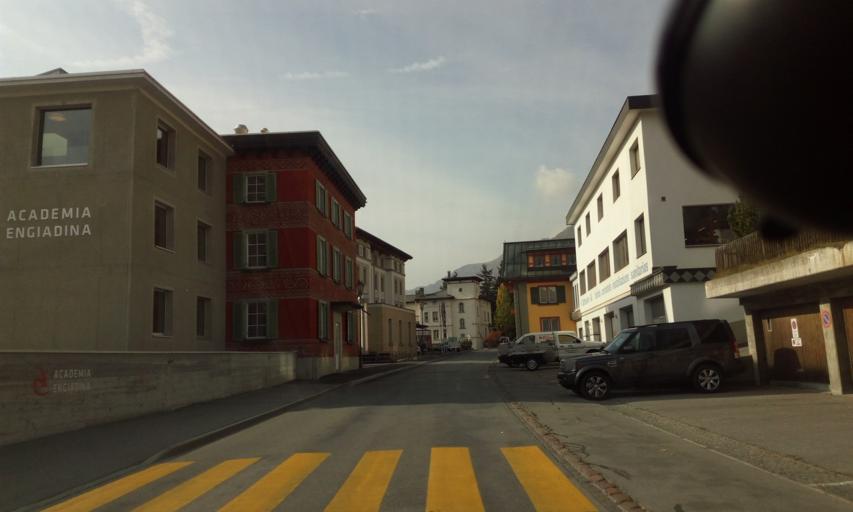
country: CH
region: Grisons
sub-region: Maloja District
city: Samedan
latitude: 46.5375
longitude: 9.8758
